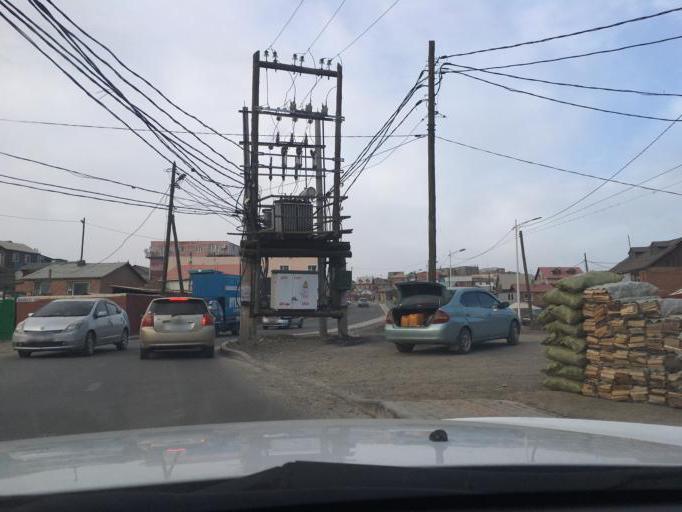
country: MN
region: Ulaanbaatar
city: Ulaanbaatar
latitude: 47.9210
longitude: 106.8526
